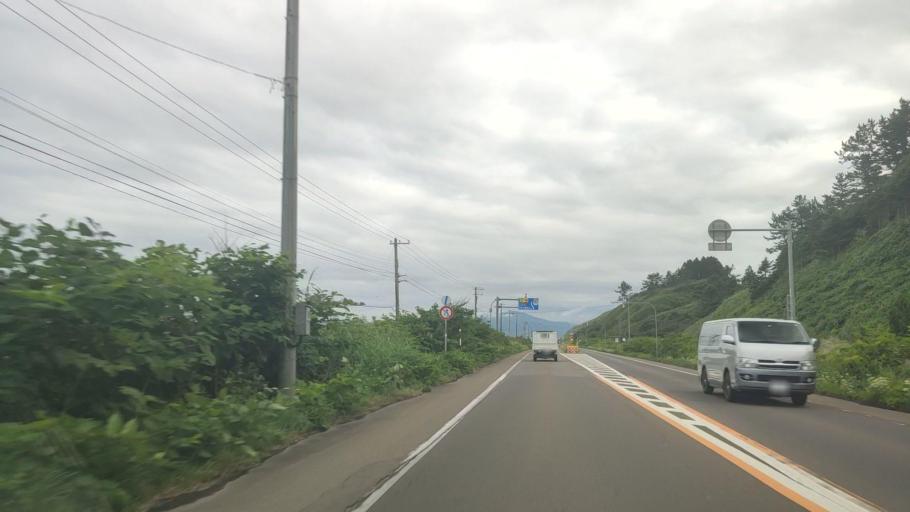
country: JP
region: Hokkaido
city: Niseko Town
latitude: 42.3336
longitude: 140.2787
